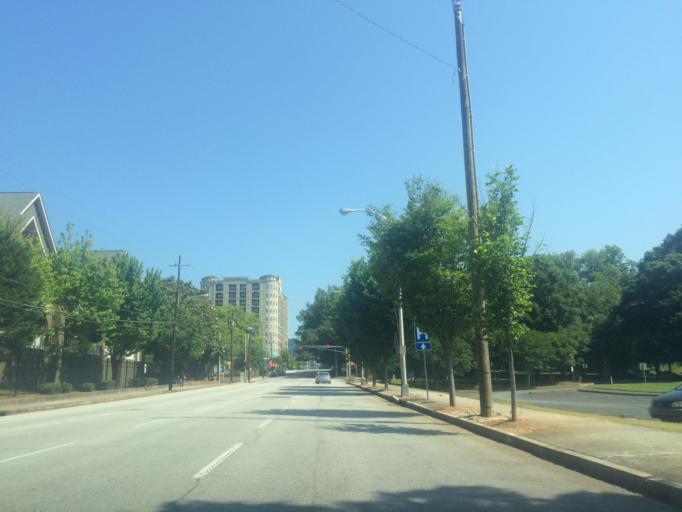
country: US
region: Georgia
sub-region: Fulton County
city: Atlanta
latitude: 33.7666
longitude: -84.3820
